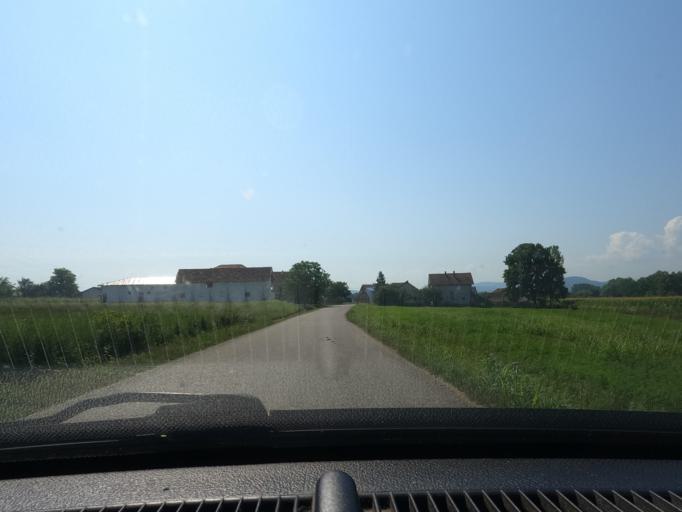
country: RS
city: Jarebice
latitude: 44.5375
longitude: 19.3715
